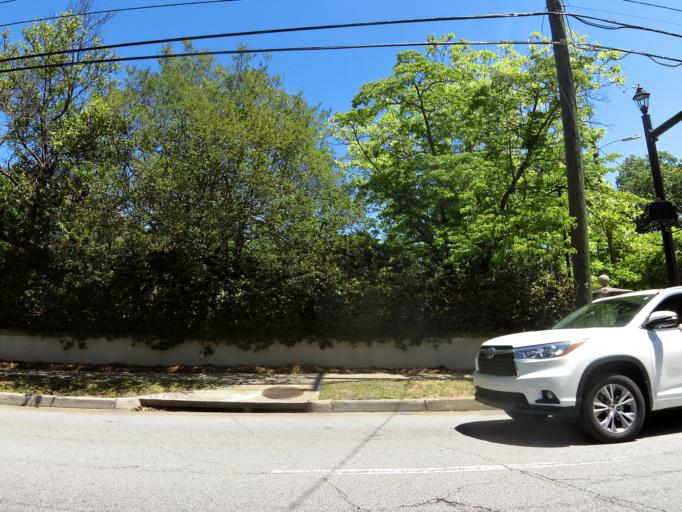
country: US
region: Georgia
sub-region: Richmond County
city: Augusta
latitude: 33.4766
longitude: -82.0131
